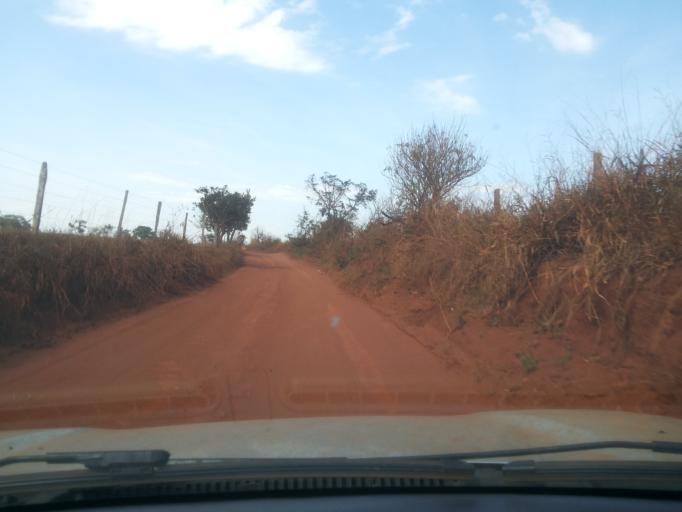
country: BR
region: Minas Gerais
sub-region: Ituiutaba
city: Ituiutaba
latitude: -19.0214
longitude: -49.3955
